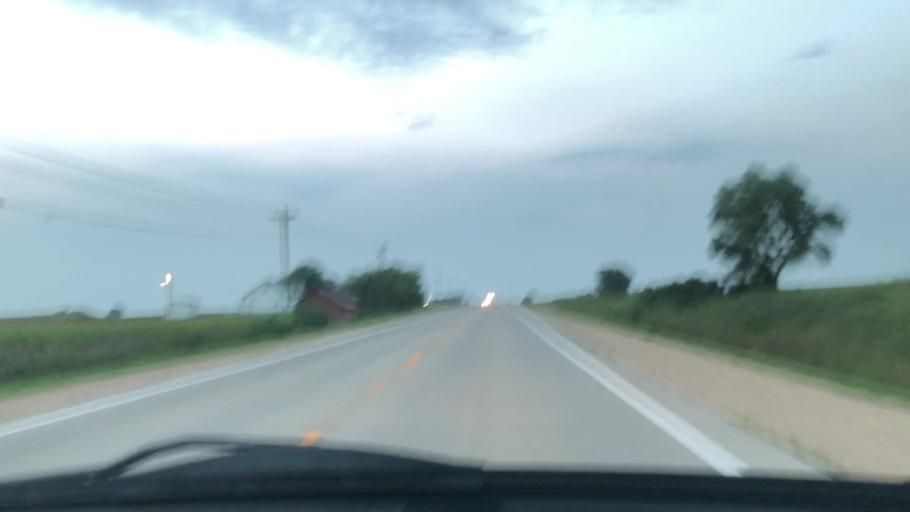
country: US
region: Iowa
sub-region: Linn County
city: Ely
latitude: 41.8562
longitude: -91.6754
